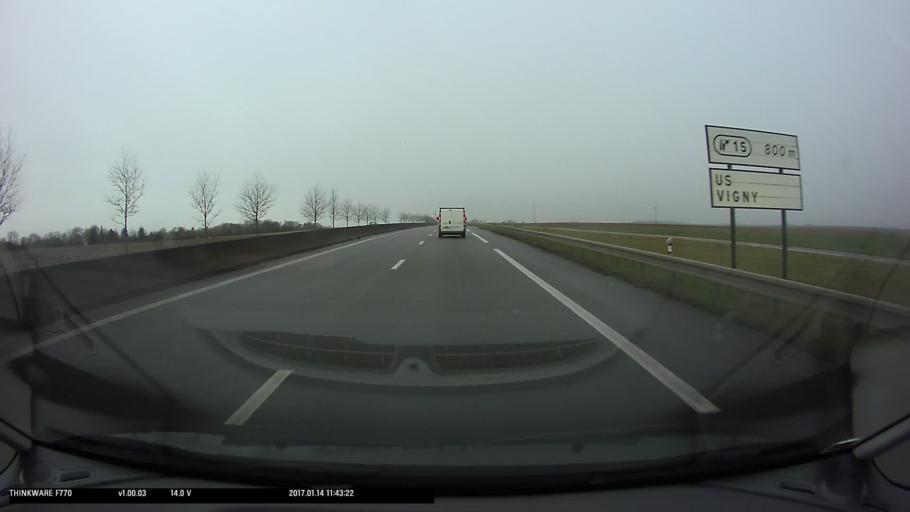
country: FR
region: Ile-de-France
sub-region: Departement du Val-d'Oise
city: Vigny
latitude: 49.0773
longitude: 1.9446
